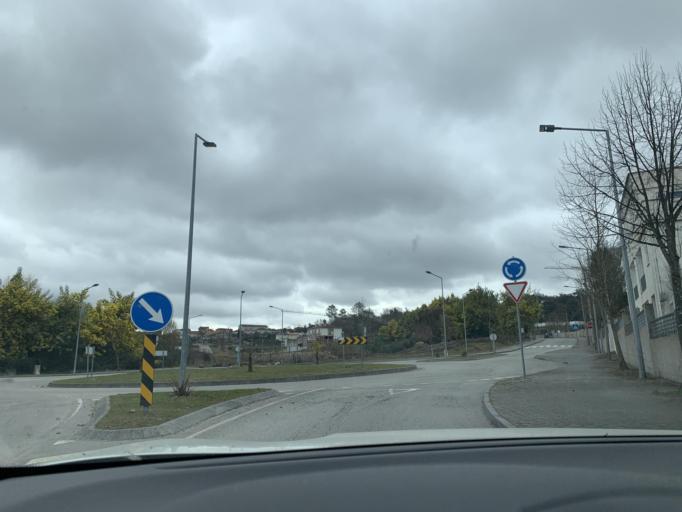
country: PT
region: Viseu
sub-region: Mangualde
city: Mangualde
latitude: 40.6106
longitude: -7.7715
